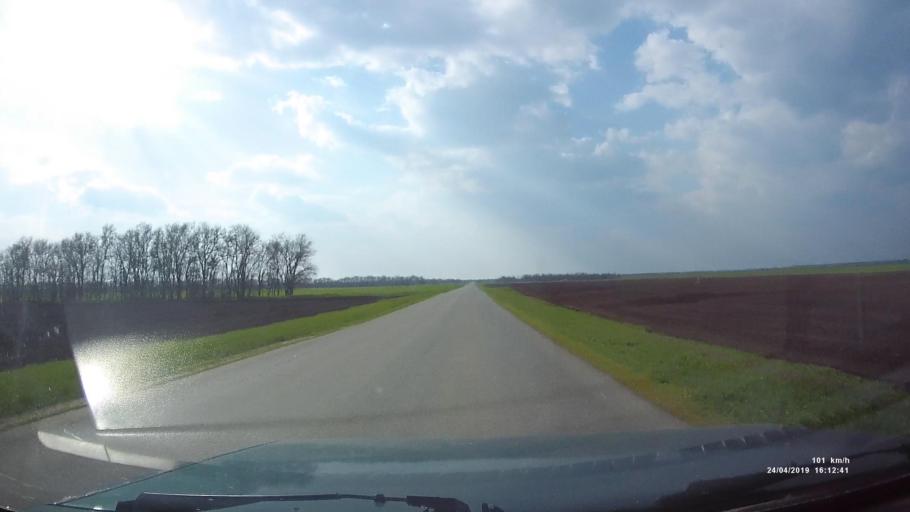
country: RU
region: Rostov
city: Sovetskoye
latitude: 46.7349
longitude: 42.2324
